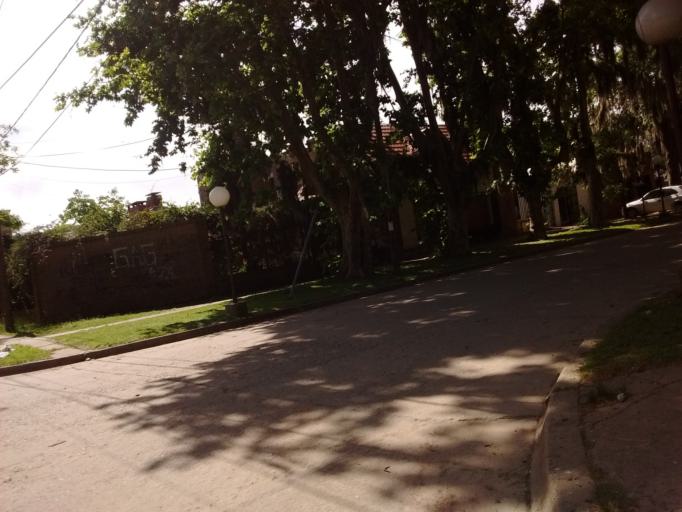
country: AR
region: Santa Fe
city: Funes
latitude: -32.9165
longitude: -60.8102
